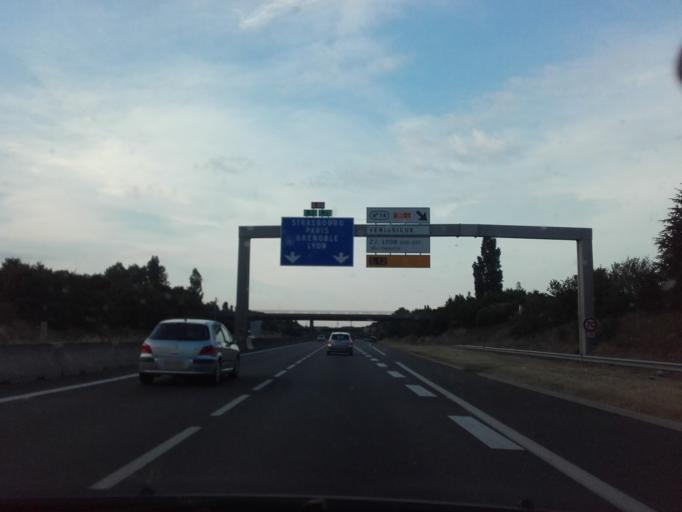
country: FR
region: Rhone-Alpes
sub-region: Departement du Rhone
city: Corbas
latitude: 45.6583
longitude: 4.9222
